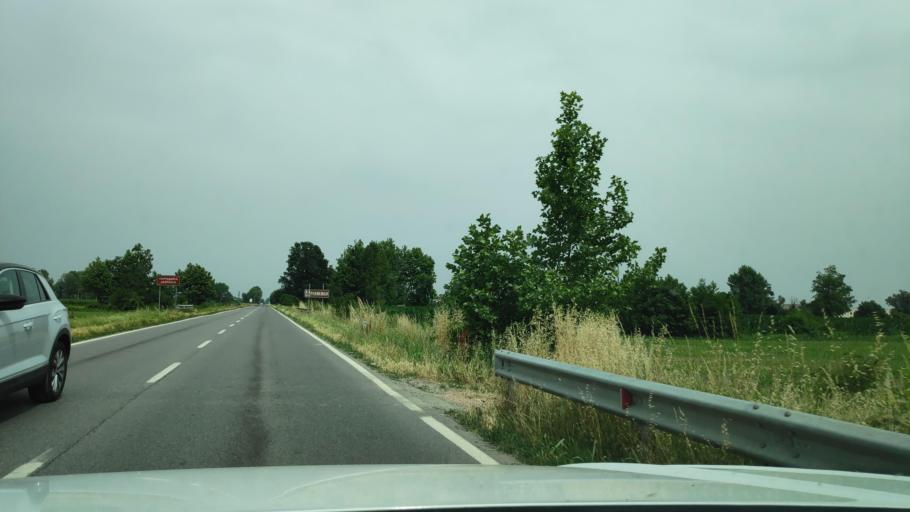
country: IT
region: Lombardy
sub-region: Provincia di Cremona
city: Pianengo
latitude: 45.4096
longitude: 9.6840
